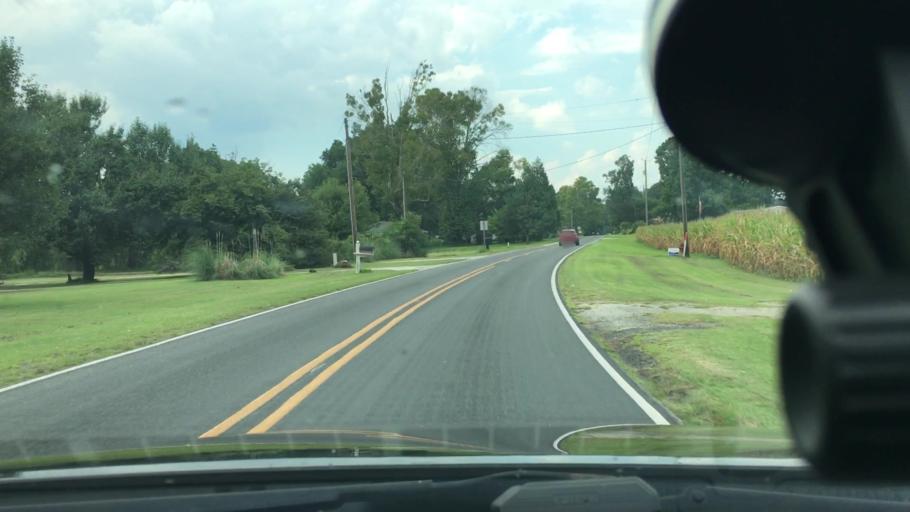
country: US
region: North Carolina
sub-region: Craven County
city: New Bern
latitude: 35.1604
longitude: -77.0465
